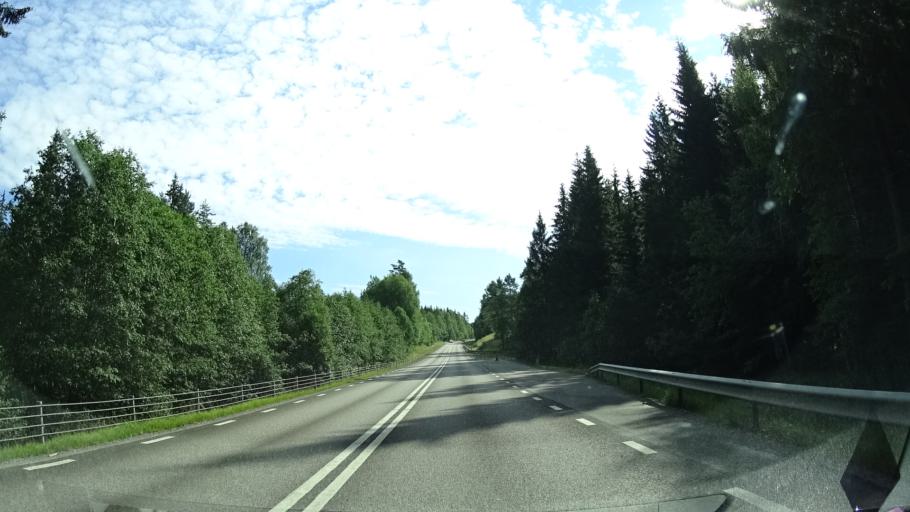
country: SE
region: Vaermland
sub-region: Arjangs Kommun
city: Toecksfors
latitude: 59.4969
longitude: 11.8915
